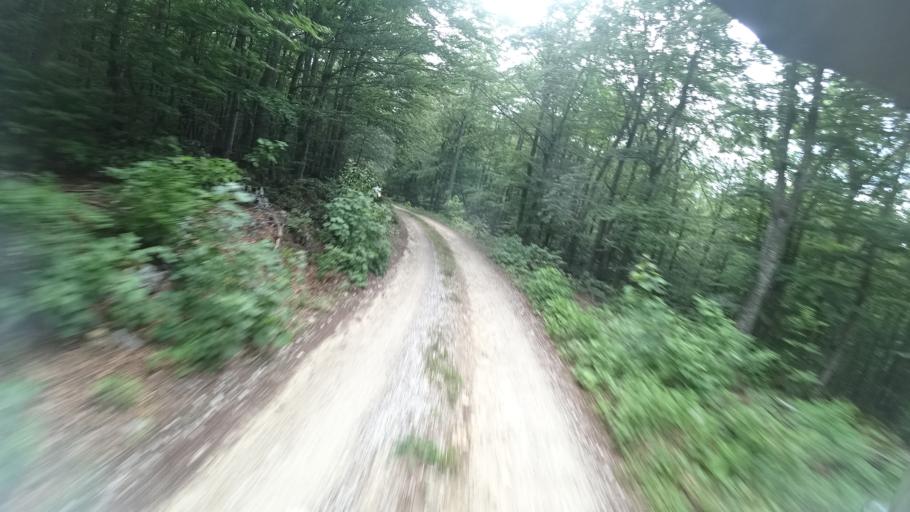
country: BA
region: Federation of Bosnia and Herzegovina
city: Bihac
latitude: 44.7346
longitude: 15.7907
